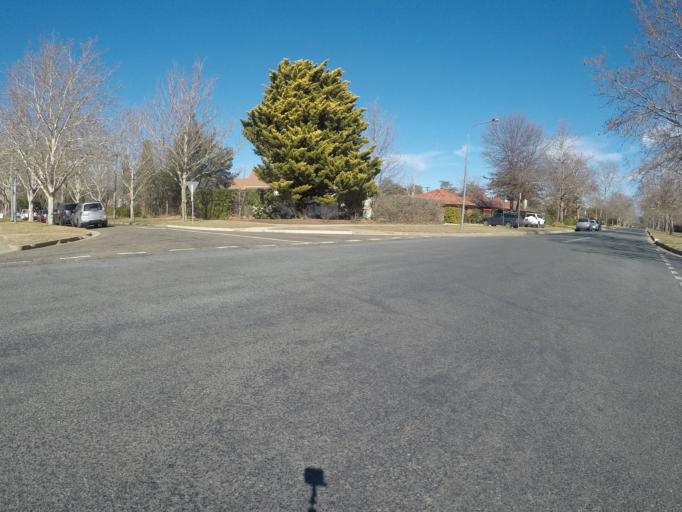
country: AU
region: Australian Capital Territory
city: Canberra
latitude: -35.2803
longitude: 149.1398
